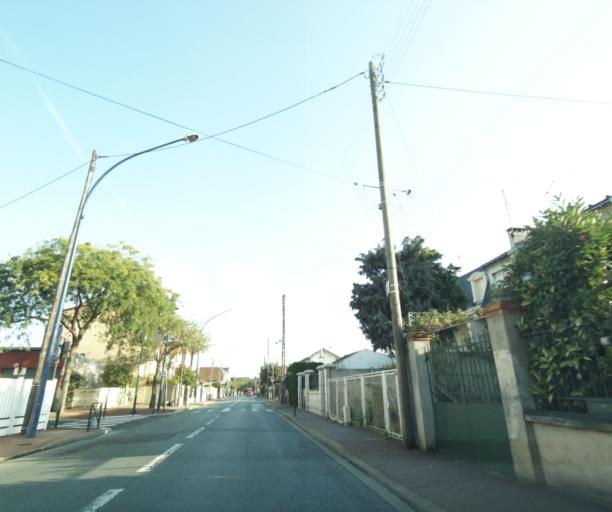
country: FR
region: Ile-de-France
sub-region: Departement de l'Essonne
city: Bievres
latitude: 48.7802
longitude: 2.2277
